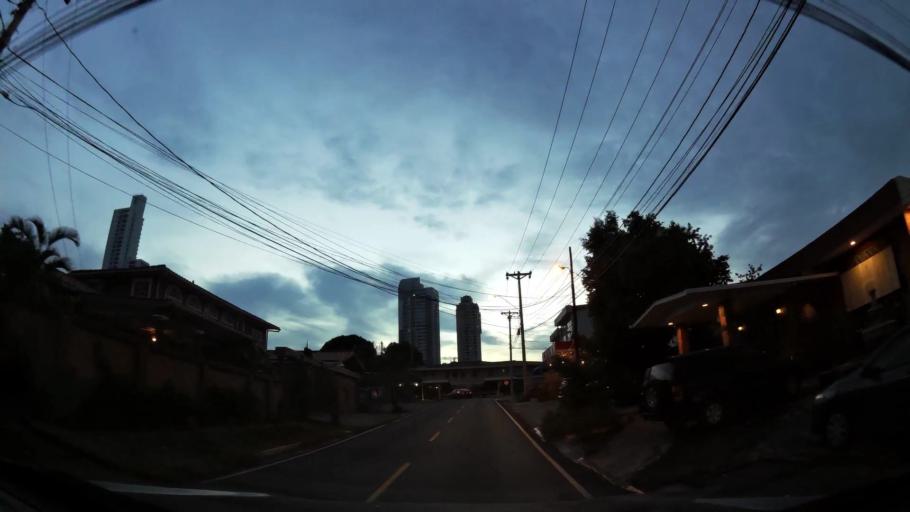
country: PA
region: Panama
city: Panama
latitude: 8.9896
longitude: -79.5072
